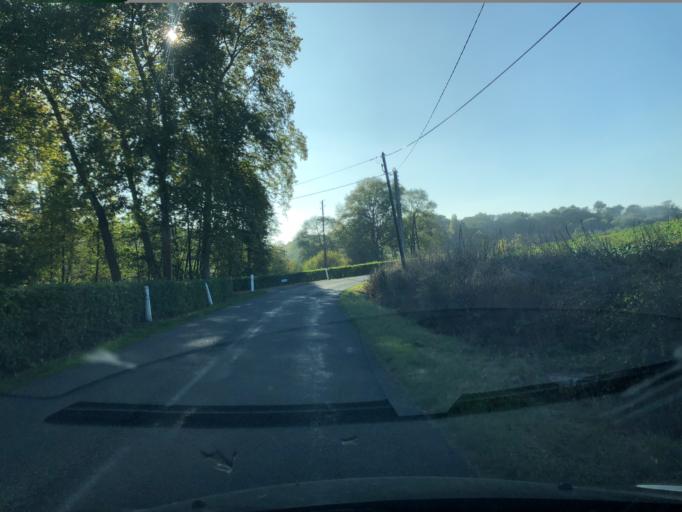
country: FR
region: Centre
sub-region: Departement d'Indre-et-Loire
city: Neuvy-le-Roi
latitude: 47.6659
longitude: 0.6256
